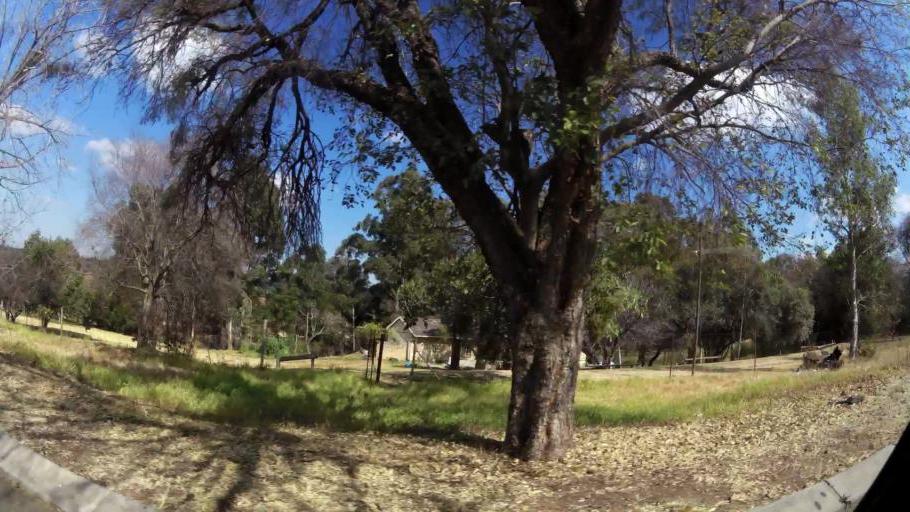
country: ZA
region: Gauteng
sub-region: West Rand District Municipality
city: Muldersdriseloop
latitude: -26.0676
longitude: 27.9593
